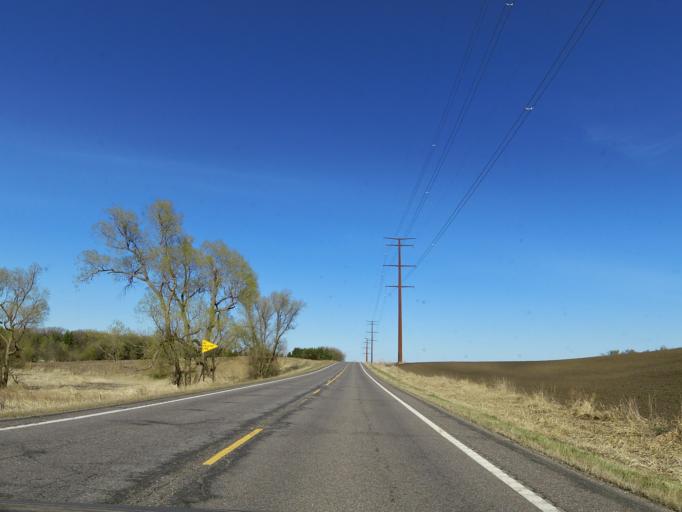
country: US
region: Minnesota
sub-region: Scott County
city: Elko New Market
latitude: 44.5728
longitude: -93.4091
